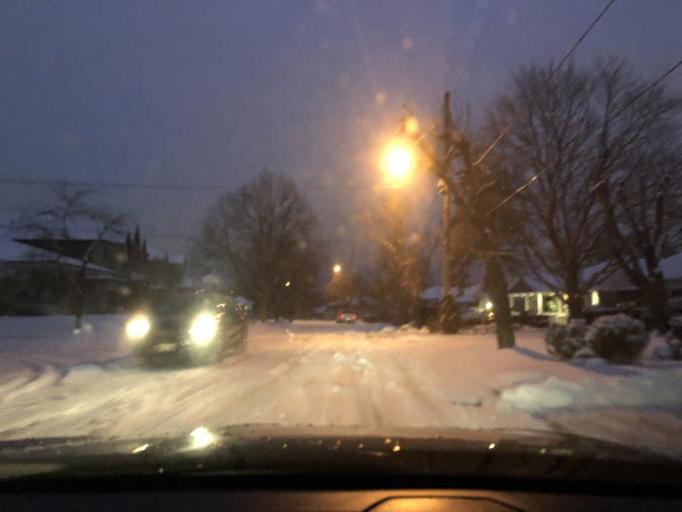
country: CA
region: Ontario
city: Toronto
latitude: 43.7030
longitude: -79.4793
